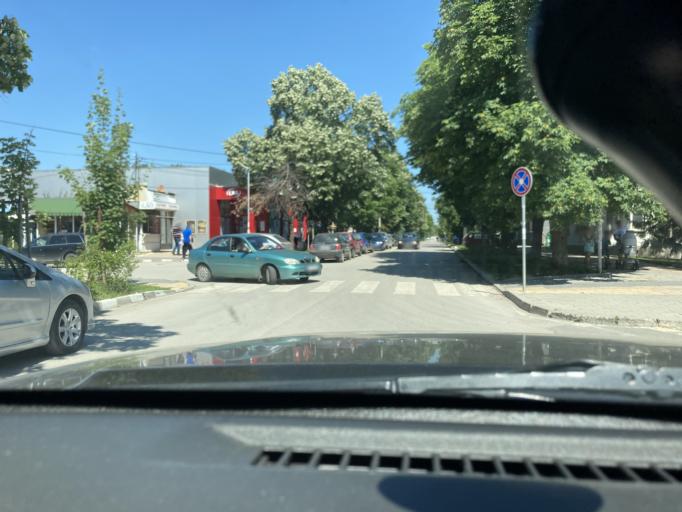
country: BG
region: Sofiya
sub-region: Obshtina Slivnitsa
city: Slivnitsa
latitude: 42.8526
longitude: 23.0378
